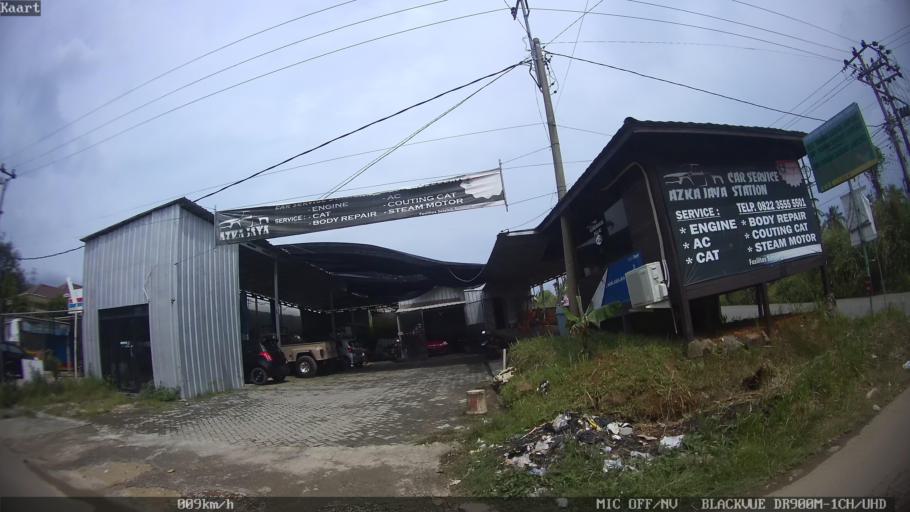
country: ID
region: Lampung
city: Bandarlampung
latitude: -5.4057
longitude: 105.1998
